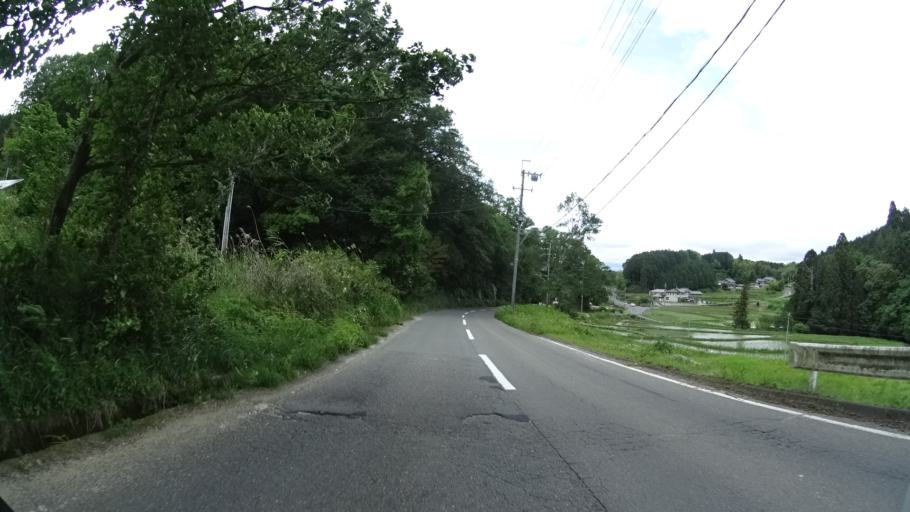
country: JP
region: Nara
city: Nara-shi
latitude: 34.7120
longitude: 135.8933
